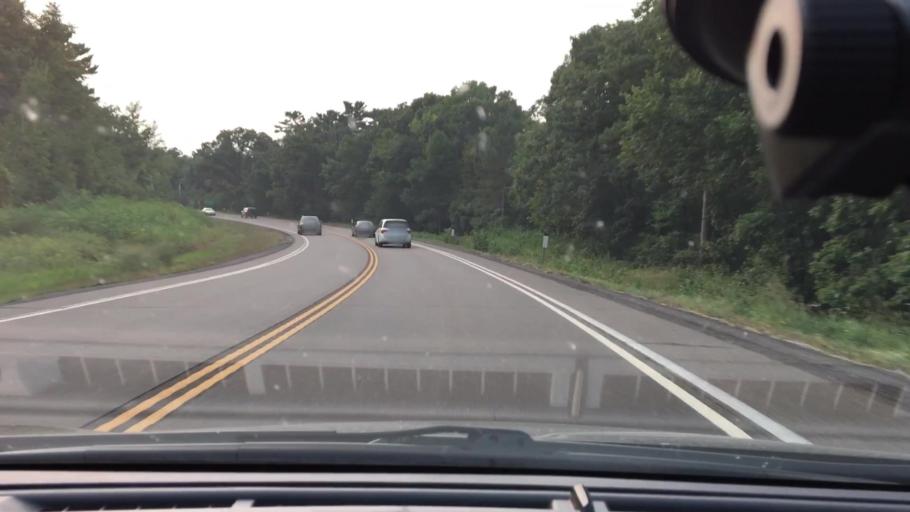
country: US
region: Minnesota
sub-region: Mille Lacs County
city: Vineland
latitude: 46.1118
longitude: -93.6469
